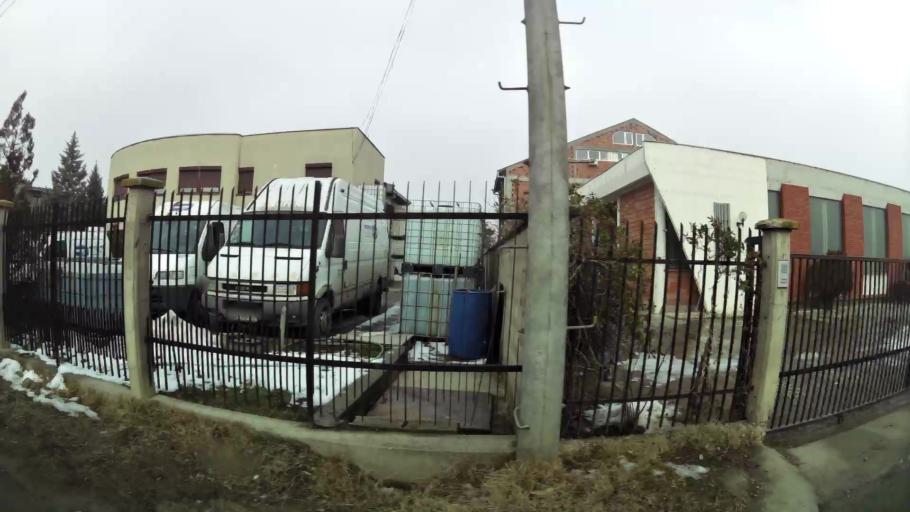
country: MK
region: Ilinden
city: Ilinden
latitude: 41.9904
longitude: 21.5770
